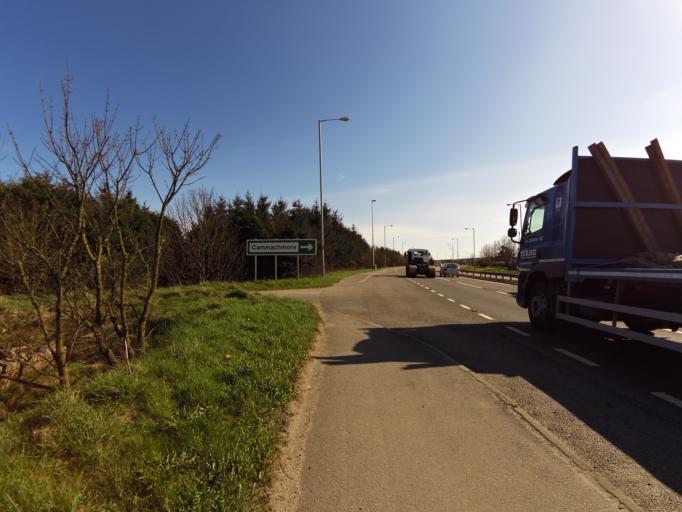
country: GB
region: Scotland
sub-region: Aberdeenshire
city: Newtonhill
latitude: 57.0497
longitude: -2.1498
